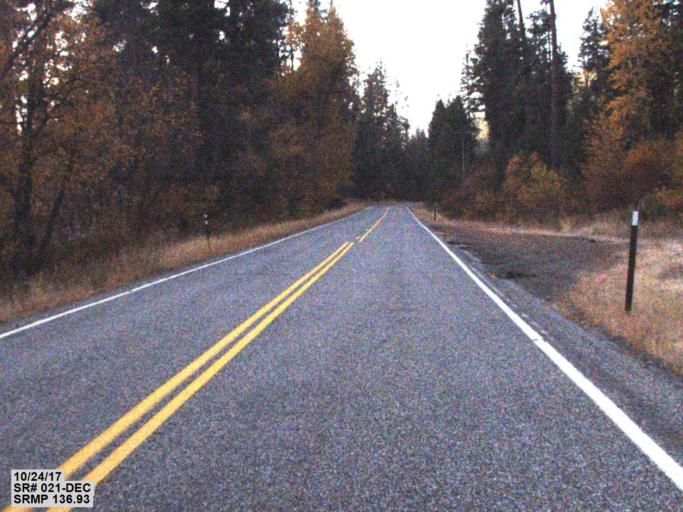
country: US
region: Washington
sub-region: Ferry County
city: Republic
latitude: 48.3475
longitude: -118.7462
